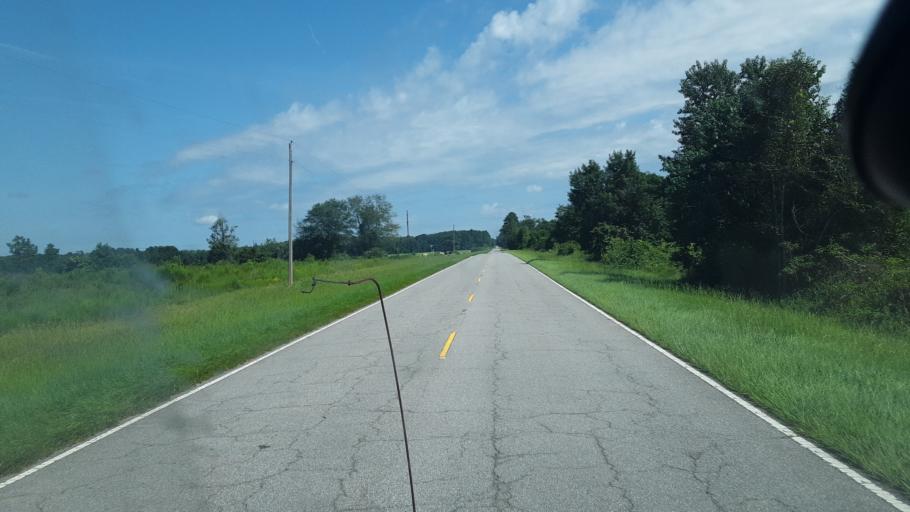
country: US
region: South Carolina
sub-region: Hampton County
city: Hampton
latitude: 33.0436
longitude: -81.0325
